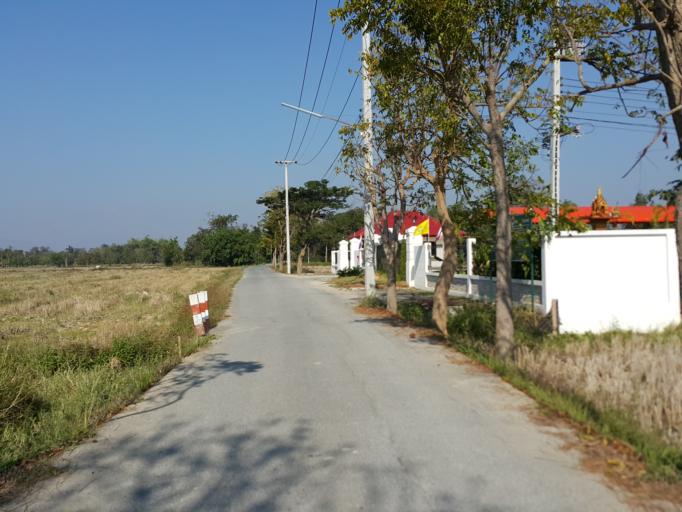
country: TH
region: Chiang Mai
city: San Kamphaeng
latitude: 18.8063
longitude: 99.0973
